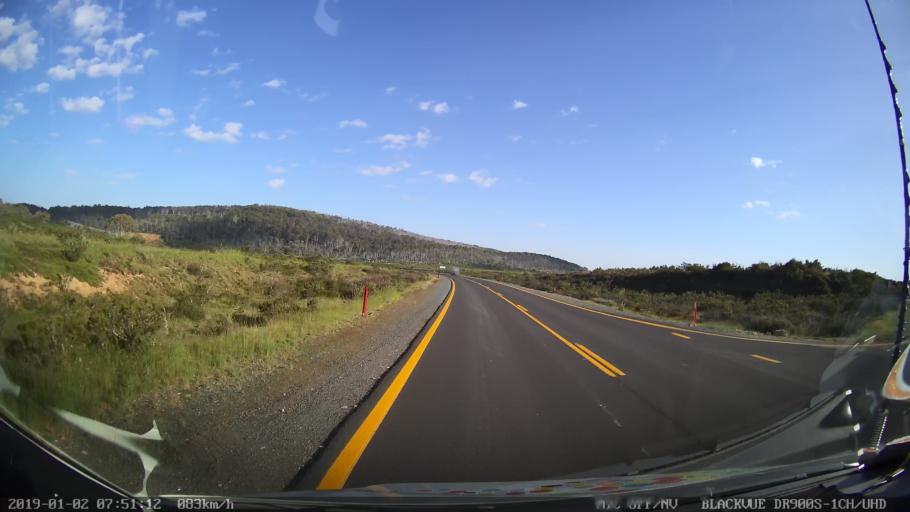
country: AU
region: New South Wales
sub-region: Tumut Shire
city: Tumut
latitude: -35.7210
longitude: 148.5312
